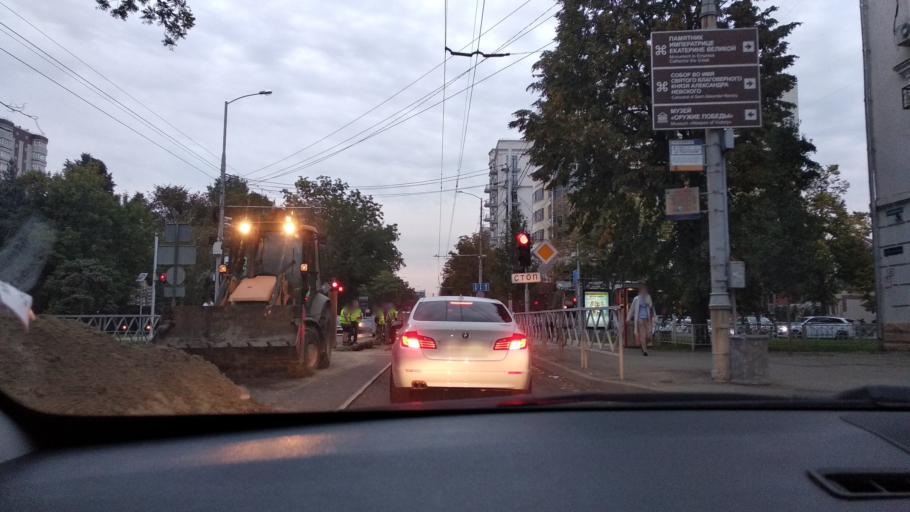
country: RU
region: Krasnodarskiy
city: Krasnodar
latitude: 45.0152
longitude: 38.9629
